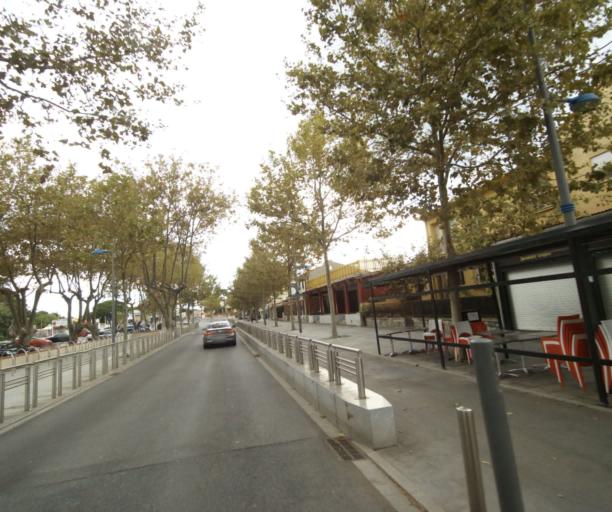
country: FR
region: Languedoc-Roussillon
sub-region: Departement des Pyrenees-Orientales
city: Argelers
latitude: 42.5520
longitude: 3.0460
